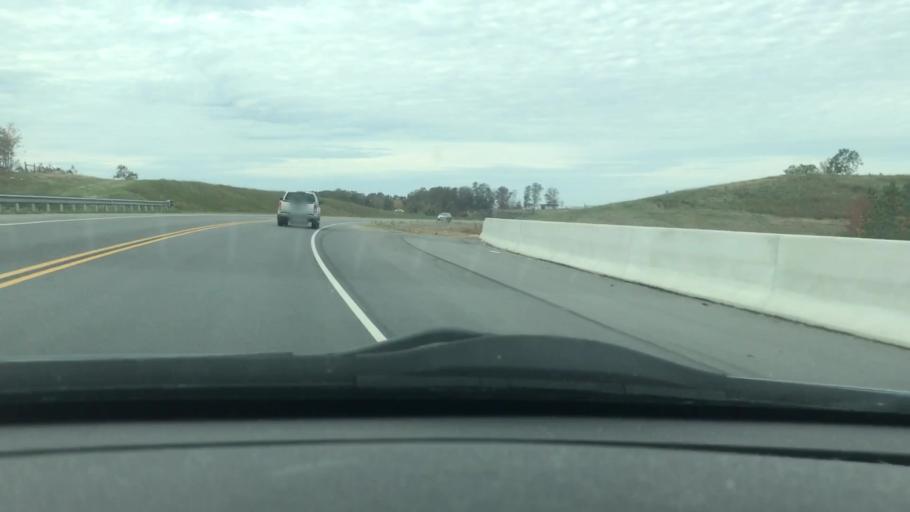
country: US
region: North Carolina
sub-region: Randolph County
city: Asheboro
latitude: 35.6976
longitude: -79.8695
